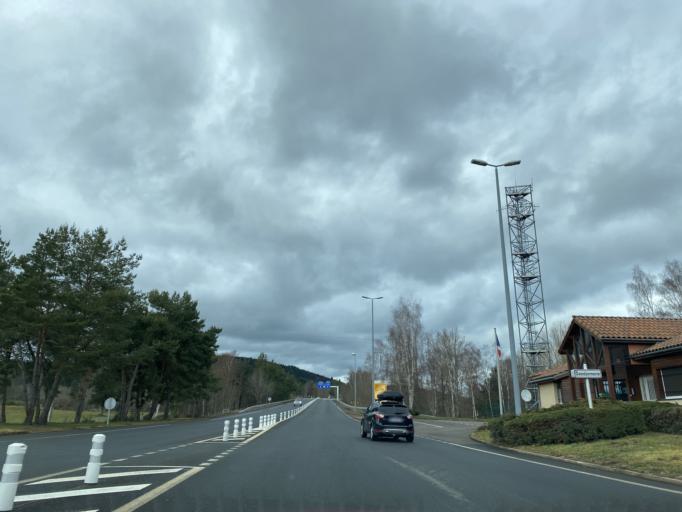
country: FR
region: Rhone-Alpes
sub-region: Departement de la Loire
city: Noiretable
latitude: 45.8497
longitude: 3.7941
